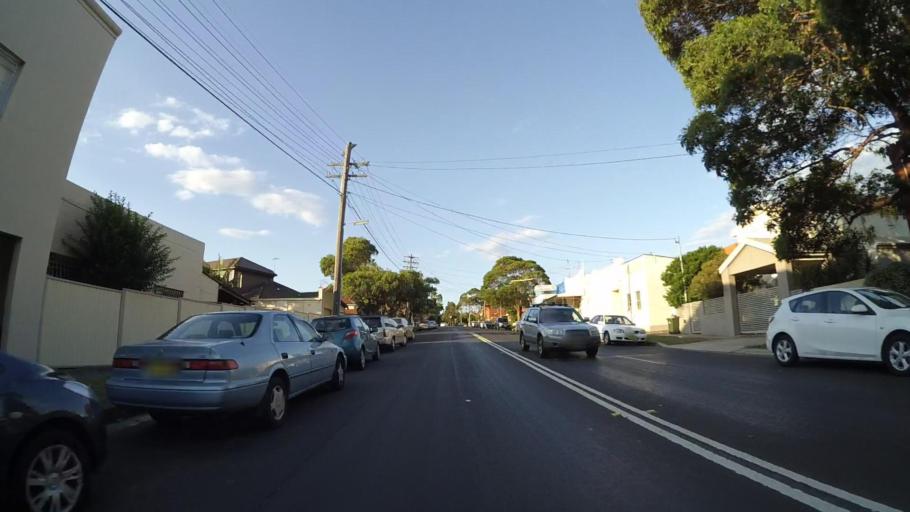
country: AU
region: New South Wales
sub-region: Randwick
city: Daceyville
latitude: -33.9277
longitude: 151.2333
